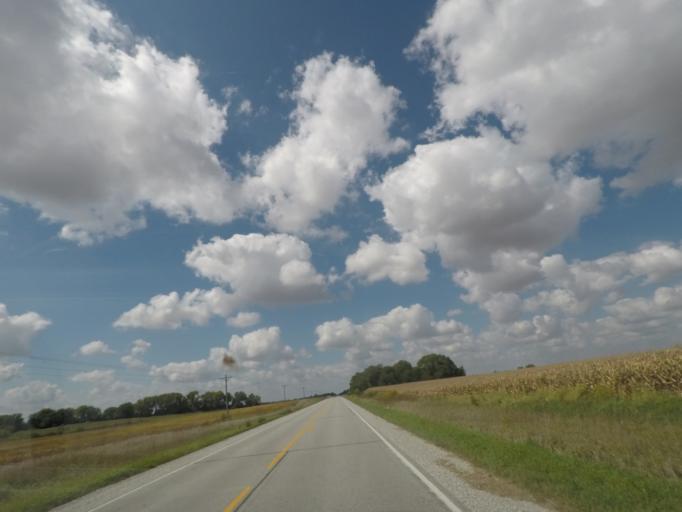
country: US
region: Iowa
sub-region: Story County
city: Nevada
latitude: 42.0226
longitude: -93.3488
